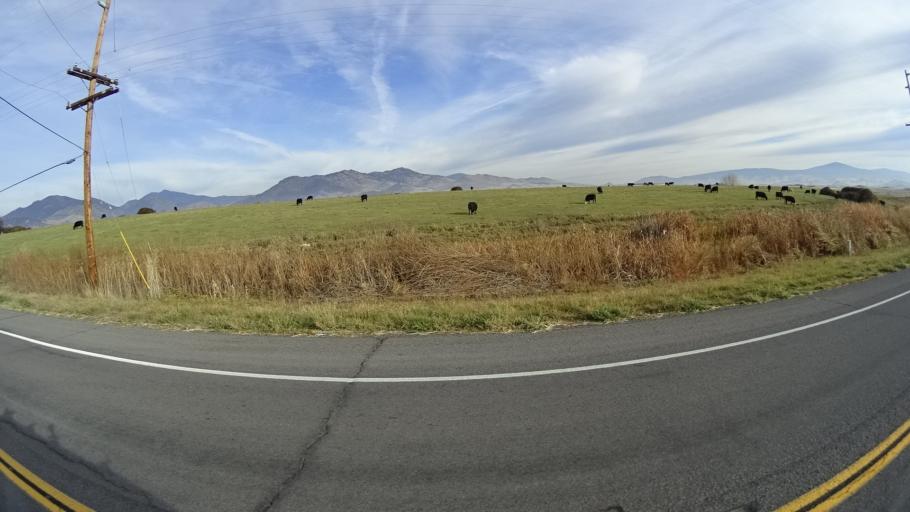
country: US
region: California
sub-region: Siskiyou County
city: Montague
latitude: 41.7291
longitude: -122.5718
